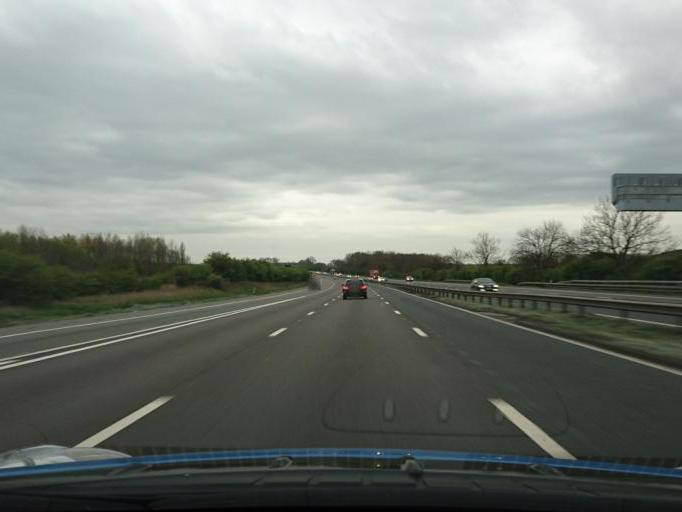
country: GB
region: England
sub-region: Staffordshire
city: Stone
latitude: 52.8728
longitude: -2.1650
